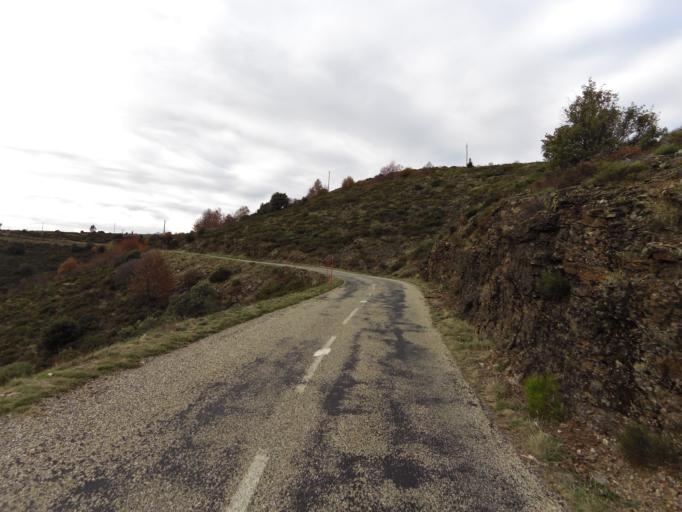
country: FR
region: Rhone-Alpes
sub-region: Departement de l'Ardeche
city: Les Vans
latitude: 44.5104
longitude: 4.0567
